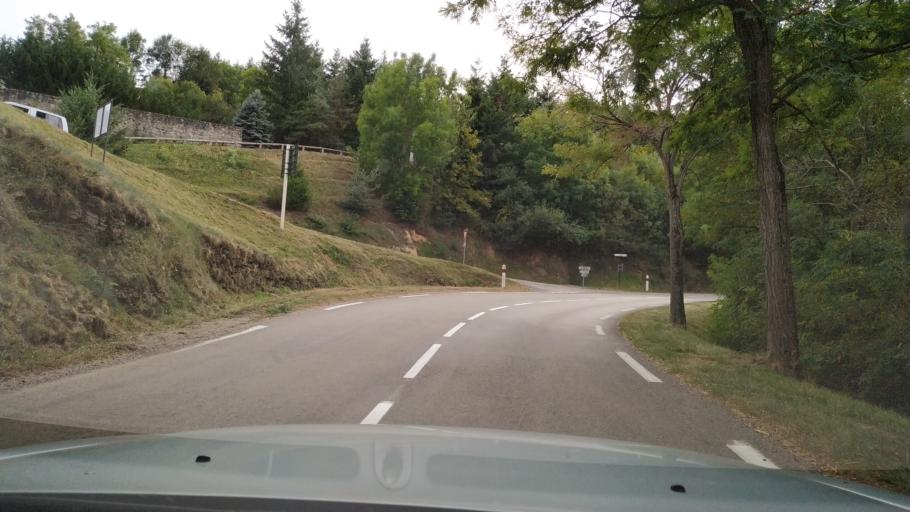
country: FR
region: Rhone-Alpes
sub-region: Departement de l'Ardeche
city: Desaignes
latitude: 44.9971
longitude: 4.5134
